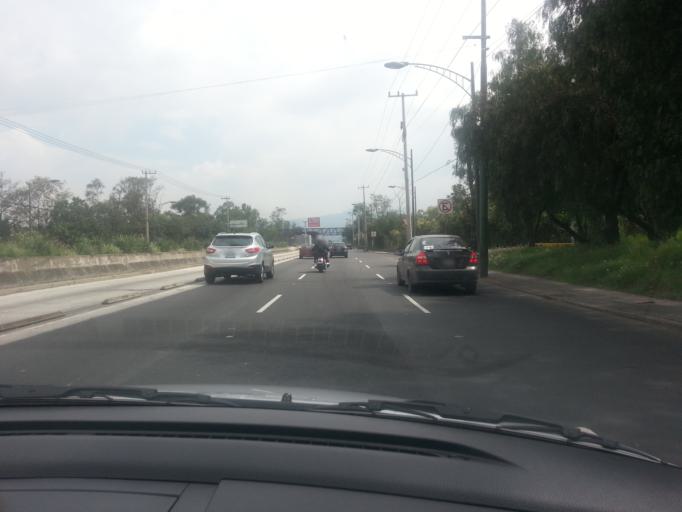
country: MX
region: Mexico City
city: Magdalena Contreras
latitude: 19.3170
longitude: -99.1878
